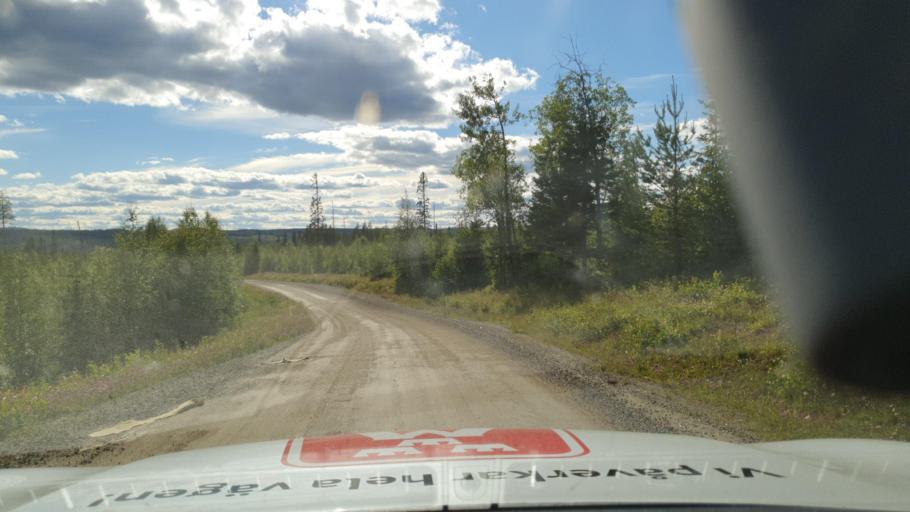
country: SE
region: Vaesterbotten
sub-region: Lycksele Kommun
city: Lycksele
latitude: 64.4070
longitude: 18.5277
